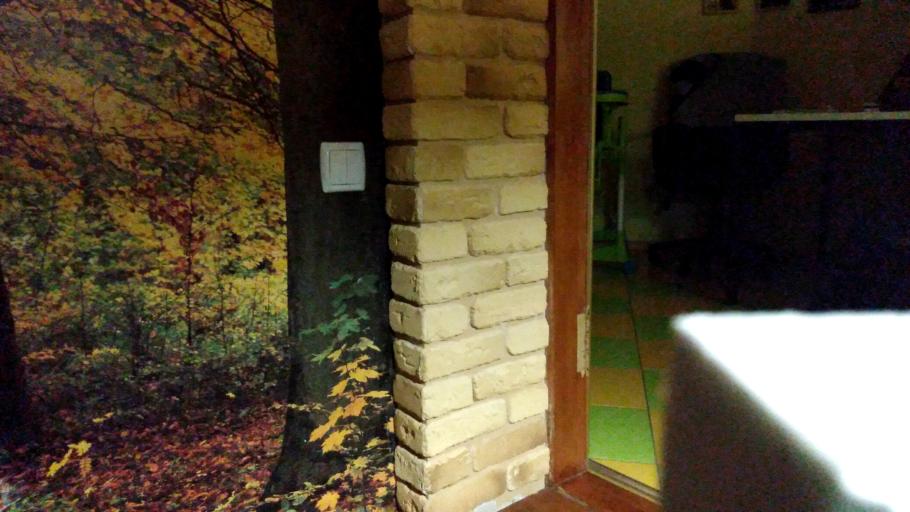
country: RU
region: Vologda
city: Lipin Bor
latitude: 61.1437
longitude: 37.9089
